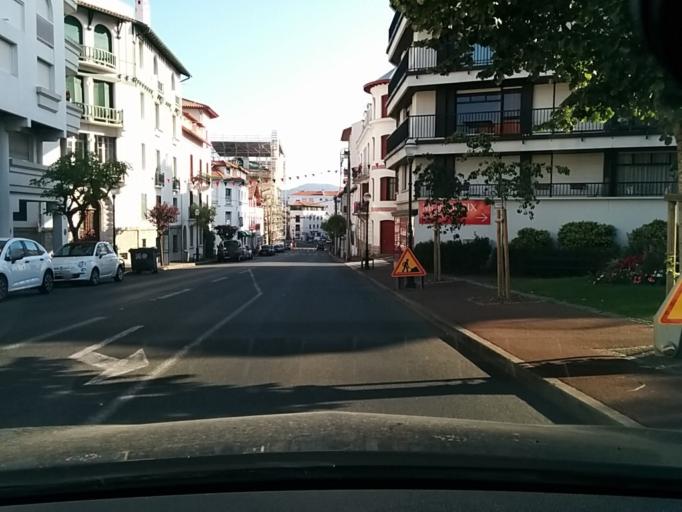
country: FR
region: Aquitaine
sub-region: Departement des Pyrenees-Atlantiques
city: Saint-Jean-de-Luz
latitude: 43.3905
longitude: -1.6573
